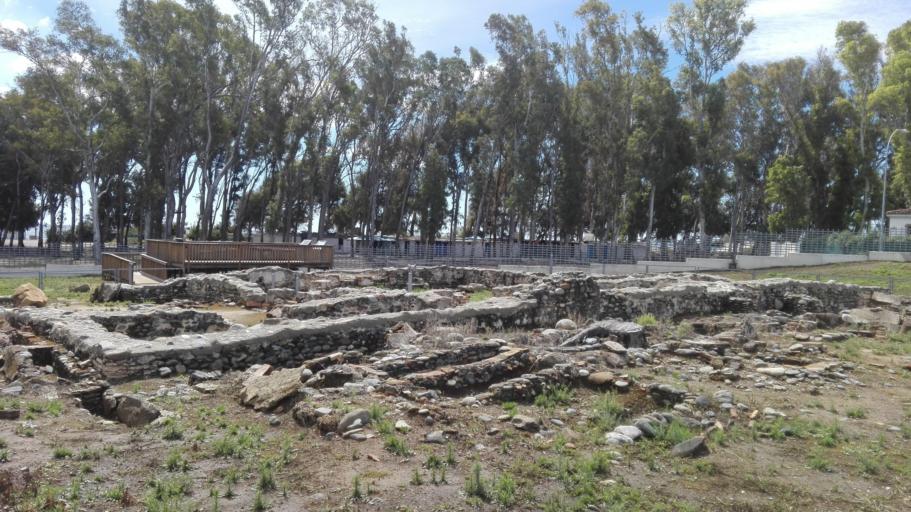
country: ES
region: Andalusia
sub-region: Provincia de Malaga
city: Benahavis
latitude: 36.4720
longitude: -4.9904
